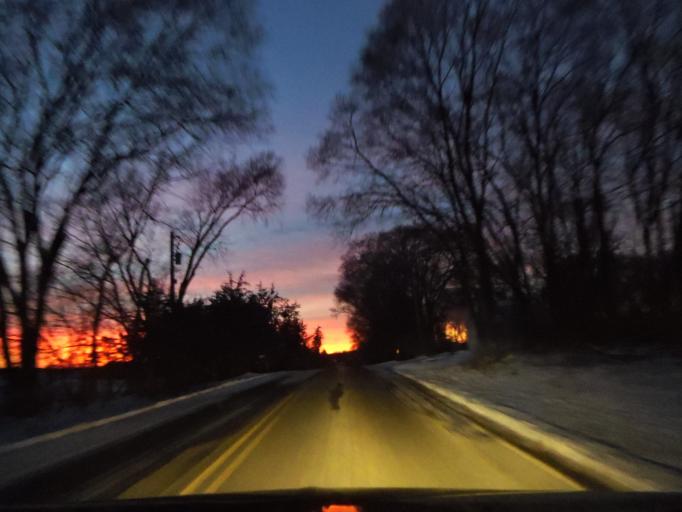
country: US
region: Minnesota
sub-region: Chisago County
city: Center City
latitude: 45.3524
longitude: -92.8112
